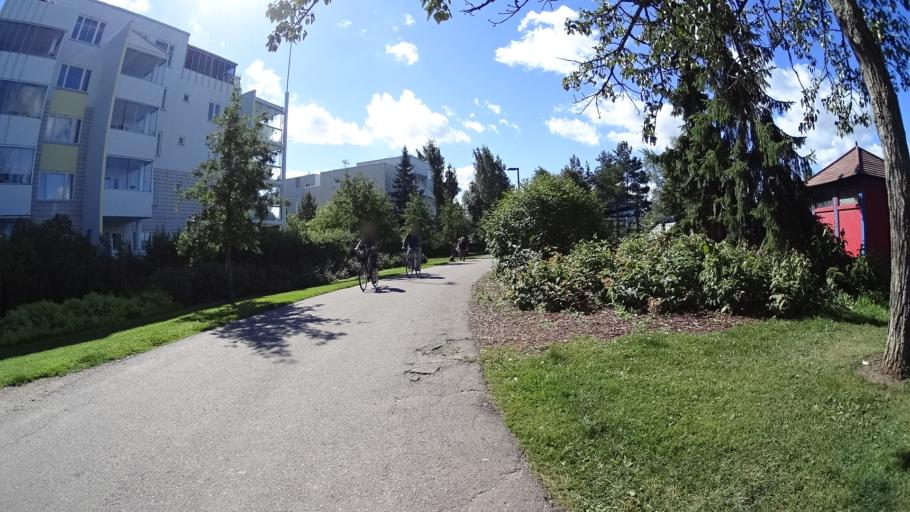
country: FI
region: Uusimaa
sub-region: Helsinki
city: Jaervenpaeae
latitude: 60.4684
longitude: 25.0846
